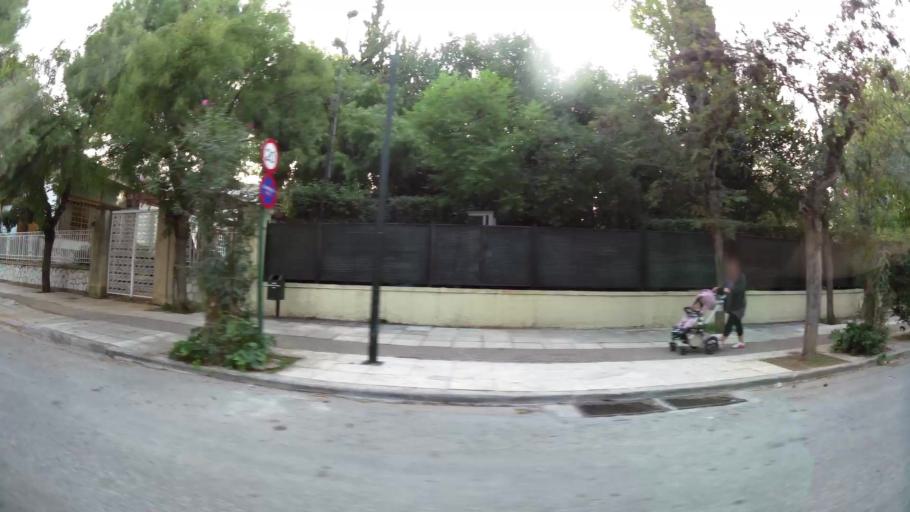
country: GR
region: Attica
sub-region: Nomarchia Athinas
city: Psychiko
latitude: 38.0086
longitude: 23.7739
